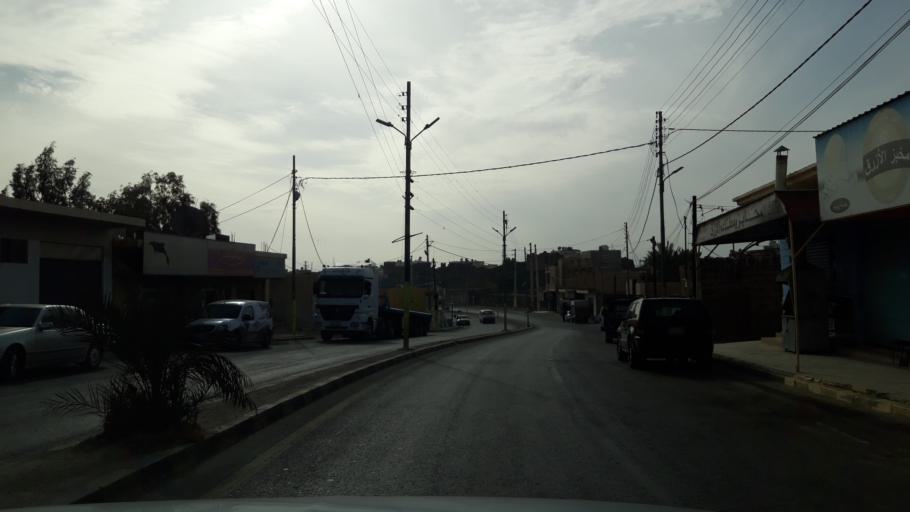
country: JO
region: Amman
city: Al Azraq ash Shamali
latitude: 31.8805
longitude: 36.8300
